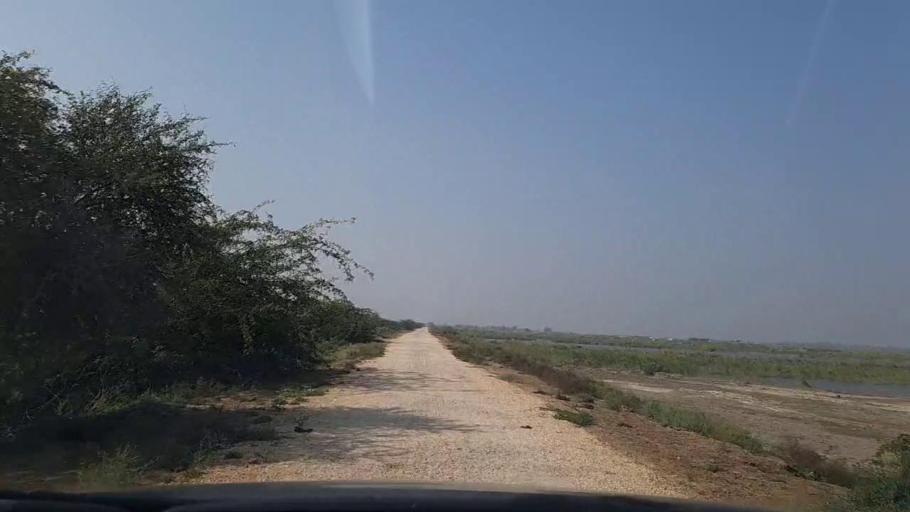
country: PK
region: Sindh
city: Mirpur Sakro
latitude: 24.5750
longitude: 67.7639
